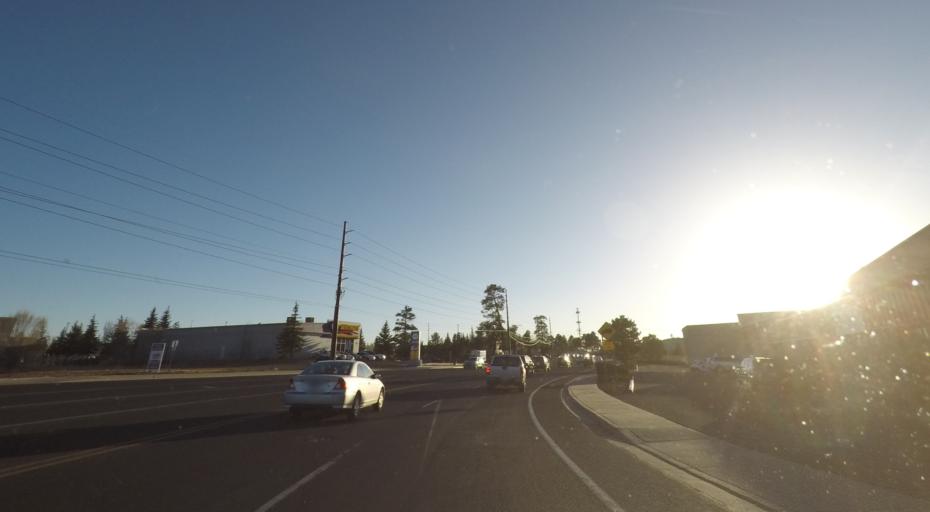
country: US
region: Arizona
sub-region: Coconino County
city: Flagstaff
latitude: 35.1919
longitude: -111.6284
